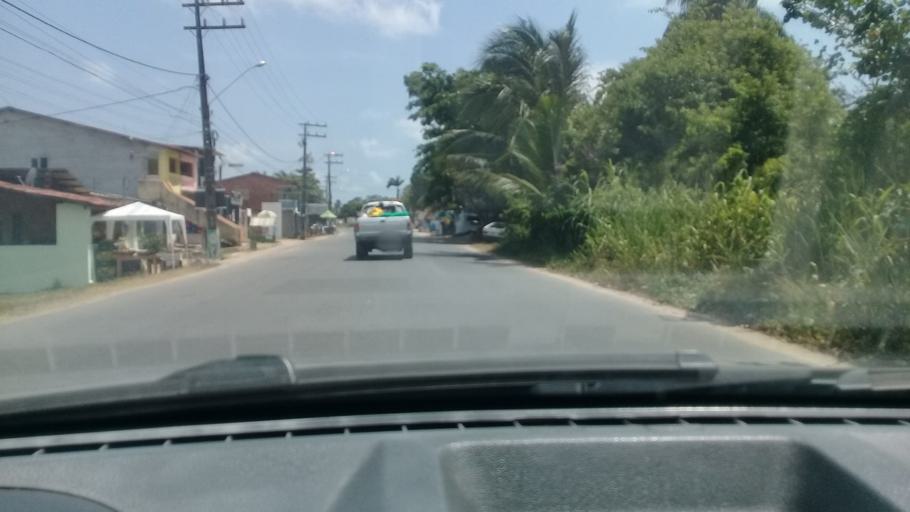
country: BR
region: Pernambuco
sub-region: Itamaraca
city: Itamaraca
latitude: -7.7725
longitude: -34.8364
